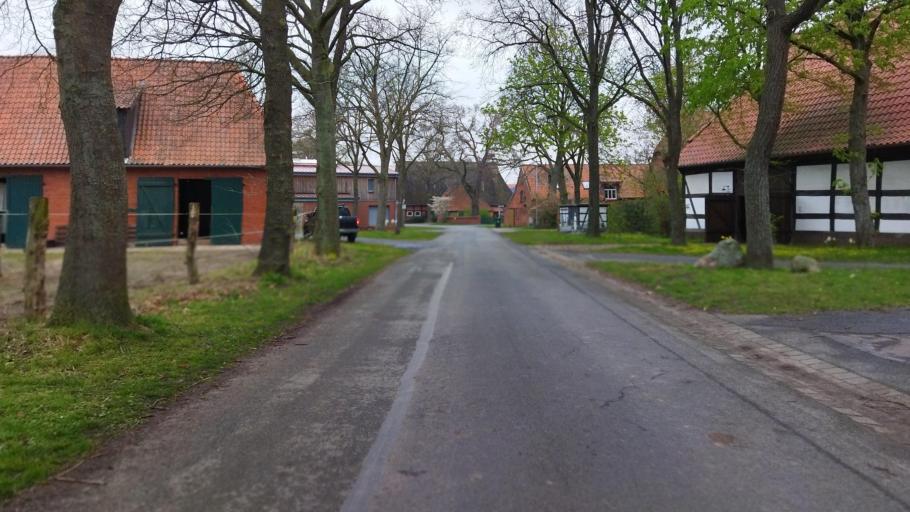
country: DE
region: Lower Saxony
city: Schweringen
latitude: 52.7458
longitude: 9.1861
